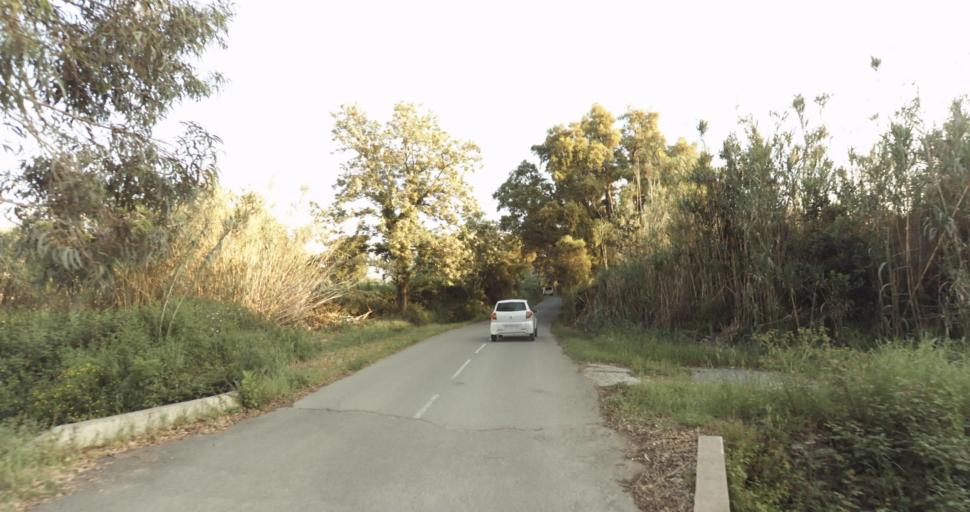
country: FR
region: Corsica
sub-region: Departement de la Haute-Corse
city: Biguglia
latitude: 42.6249
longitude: 9.4419
